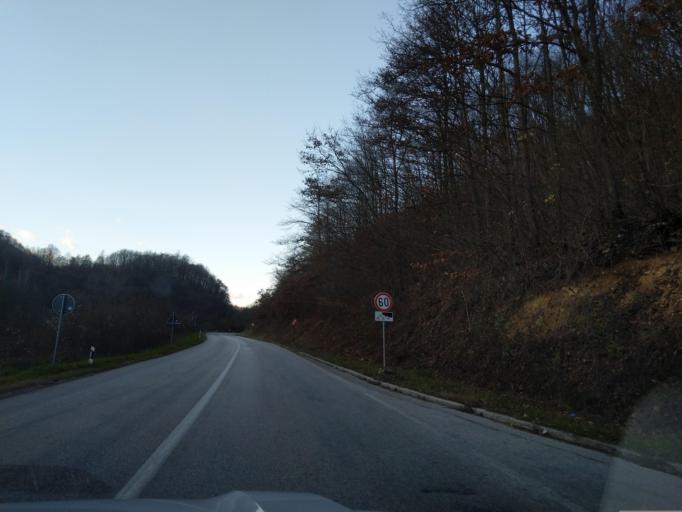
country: RS
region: Central Serbia
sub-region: Zlatiborski Okrug
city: Kosjeric
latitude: 43.9534
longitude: 19.9841
